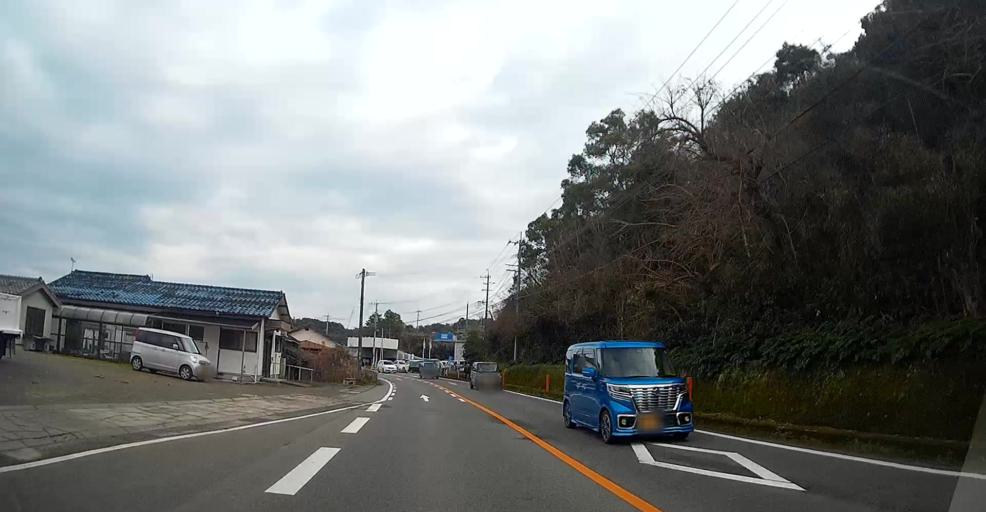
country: JP
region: Kumamoto
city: Hondo
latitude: 32.4568
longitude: 130.2217
